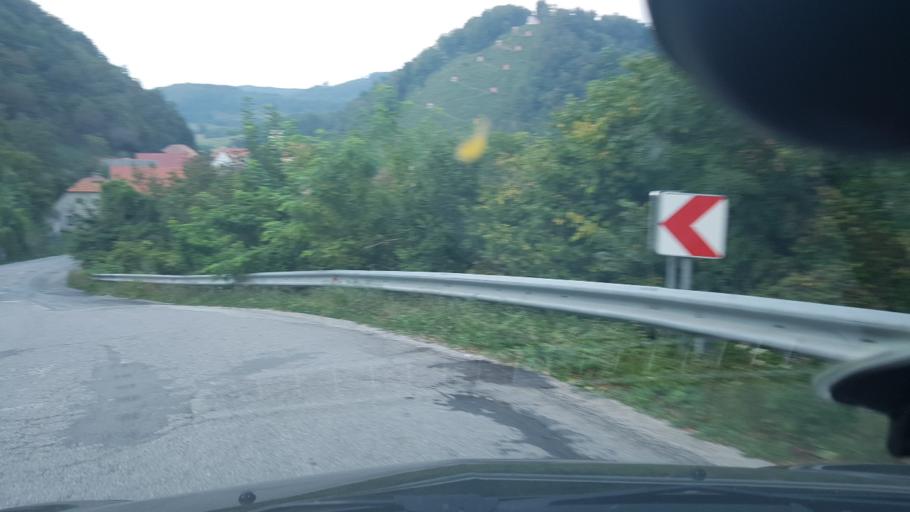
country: SI
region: Kozje
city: Kozje
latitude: 46.0385
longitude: 15.5889
